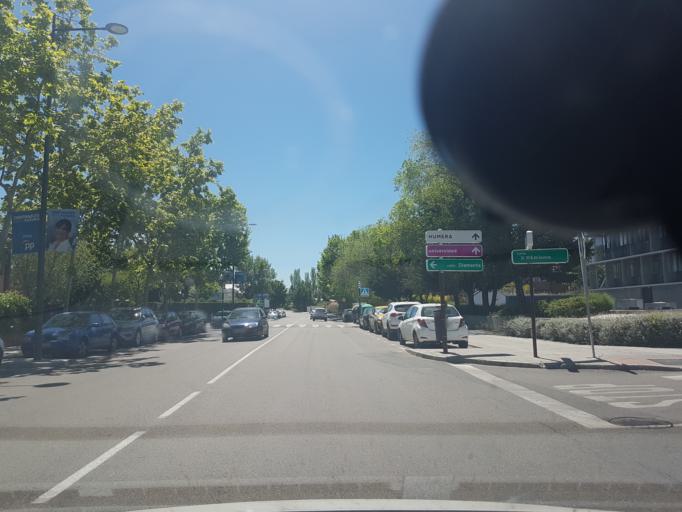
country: ES
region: Madrid
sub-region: Provincia de Madrid
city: Pozuelo de Alarcon
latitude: 40.4390
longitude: -3.8015
